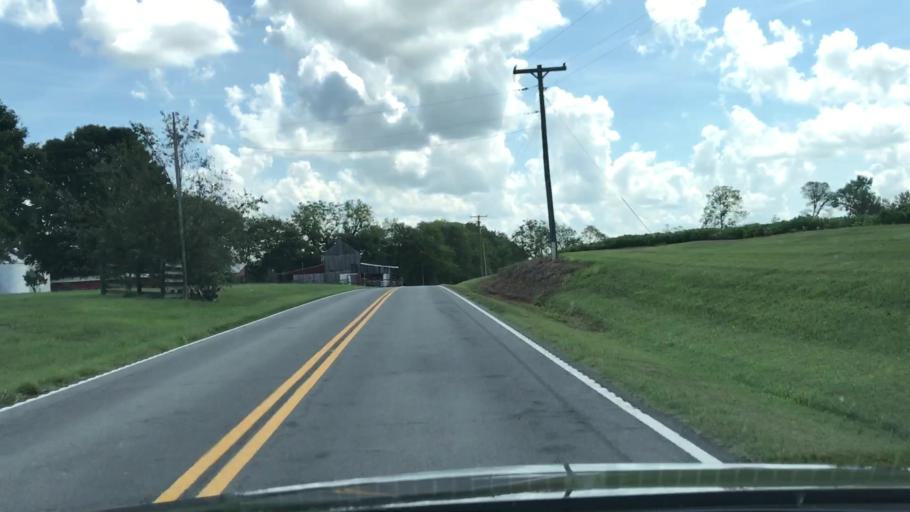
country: US
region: Tennessee
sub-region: Robertson County
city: Springfield
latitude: 36.5754
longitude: -86.8689
